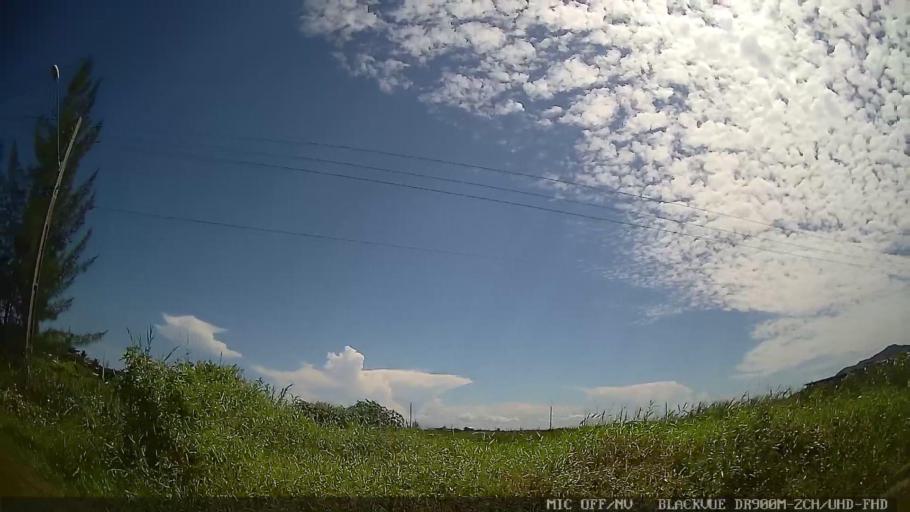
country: BR
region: Sao Paulo
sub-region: Iguape
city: Iguape
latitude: -24.7248
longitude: -47.5125
